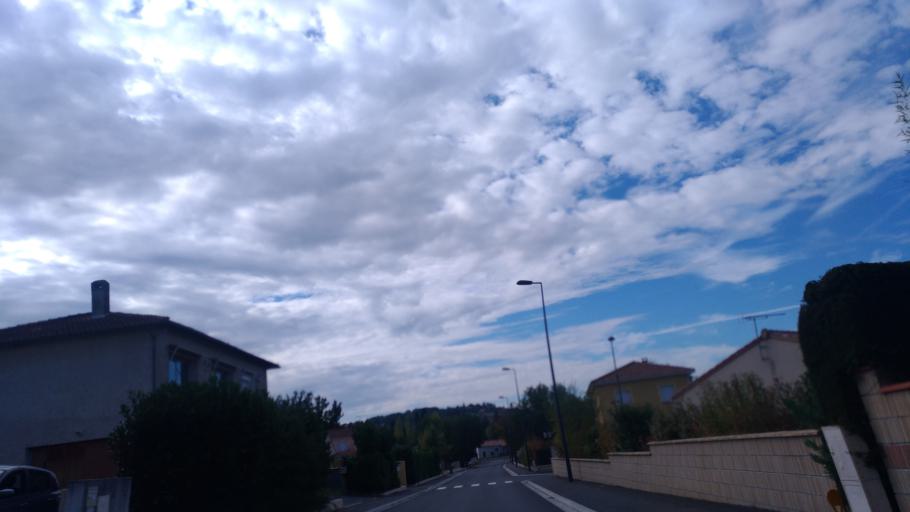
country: FR
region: Midi-Pyrenees
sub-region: Departement du Tarn
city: Puygouzon
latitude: 43.9152
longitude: 2.1761
